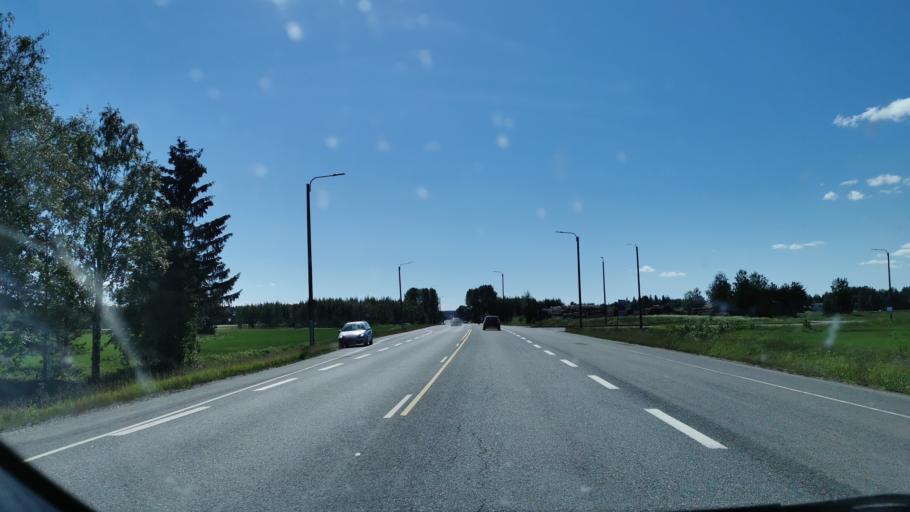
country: FI
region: Haeme
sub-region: Forssa
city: Humppila
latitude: 60.9554
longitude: 23.3471
